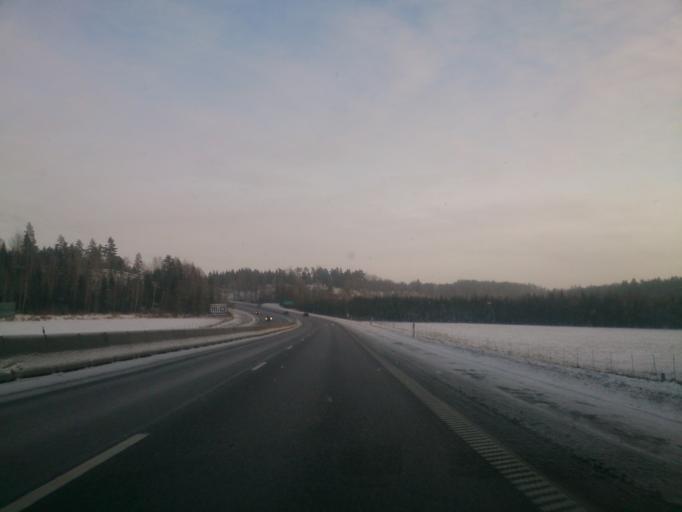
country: SE
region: OEstergoetland
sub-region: Norrkopings Kommun
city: Kimstad
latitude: 58.5309
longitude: 16.0271
